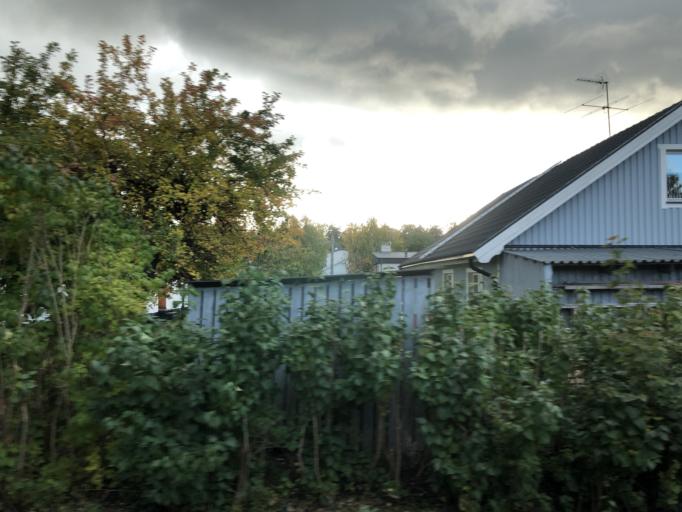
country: SE
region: Stockholm
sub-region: Jarfalla Kommun
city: Jakobsberg
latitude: 59.4282
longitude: 17.8205
